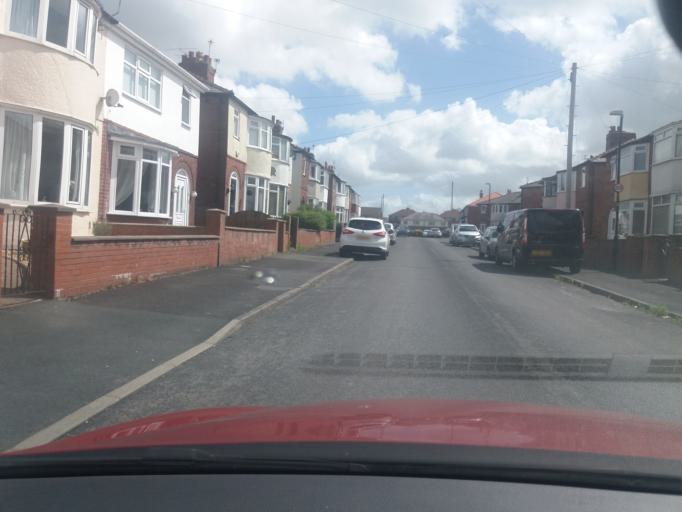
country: GB
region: England
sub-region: Lancashire
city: Chorley
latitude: 53.6430
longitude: -2.6313
